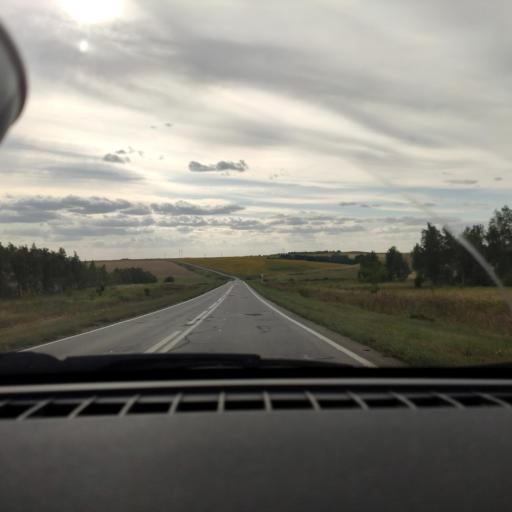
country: RU
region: Samara
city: Kinel'
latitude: 53.4415
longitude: 50.6219
